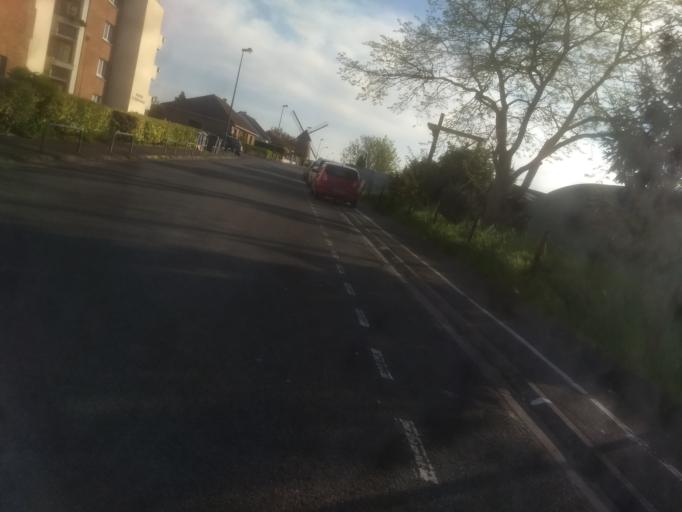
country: FR
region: Nord-Pas-de-Calais
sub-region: Departement du Pas-de-Calais
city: Achicourt
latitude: 50.2770
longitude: 2.7714
